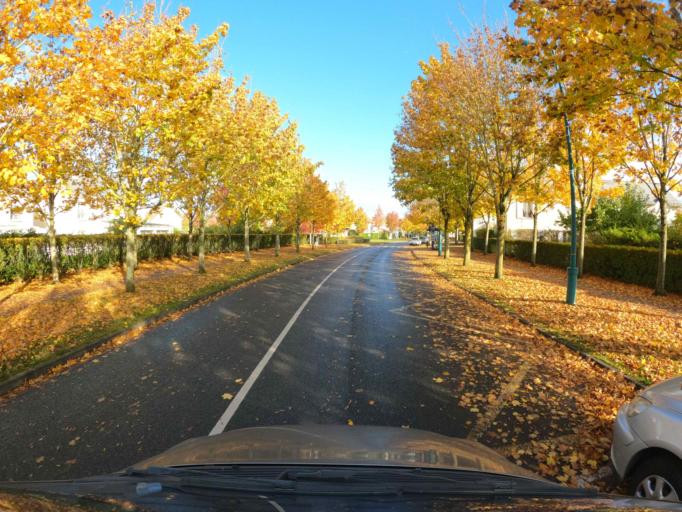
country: FR
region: Ile-de-France
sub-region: Departement de Seine-et-Marne
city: Bailly-Romainvilliers
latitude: 48.8470
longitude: 2.8160
